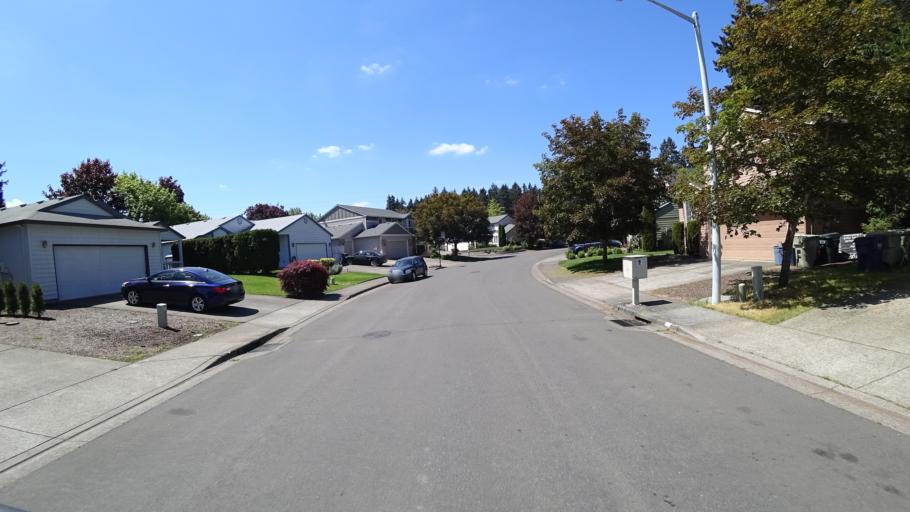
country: US
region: Oregon
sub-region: Washington County
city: Rockcreek
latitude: 45.5190
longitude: -122.8977
